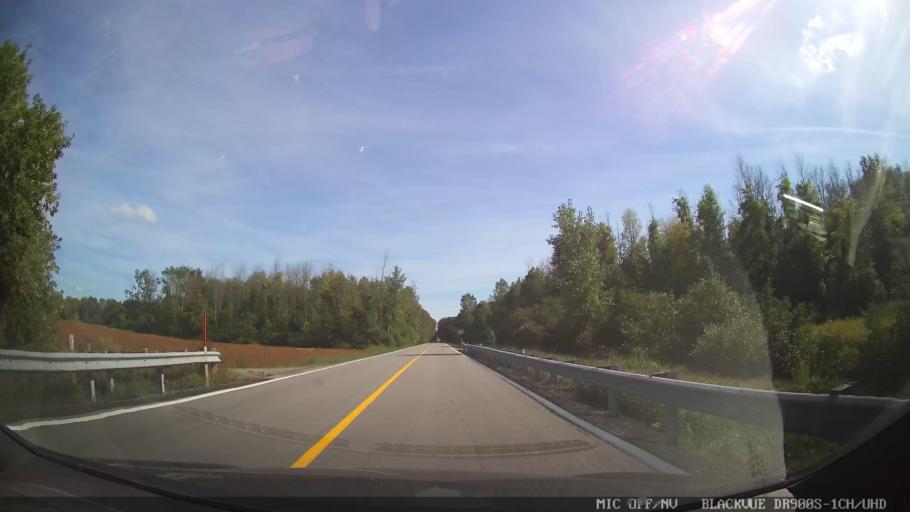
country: CA
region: Ontario
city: Bells Corners
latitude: 45.0916
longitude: -75.7024
